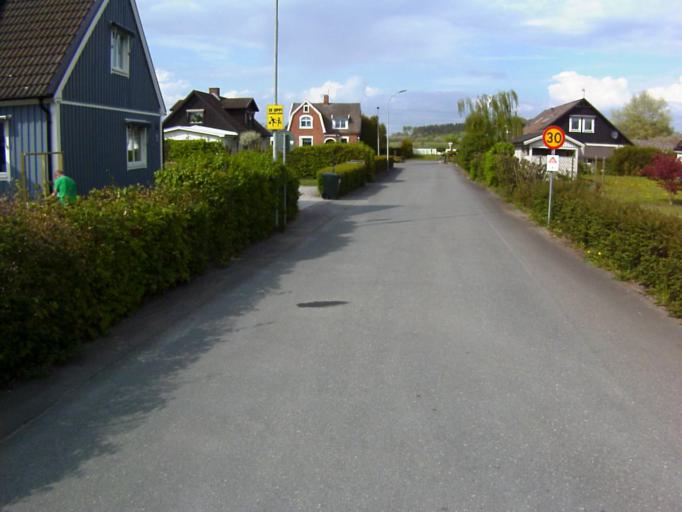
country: SE
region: Skane
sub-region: Kristianstads Kommun
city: Fjalkinge
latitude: 56.0443
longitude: 14.2708
